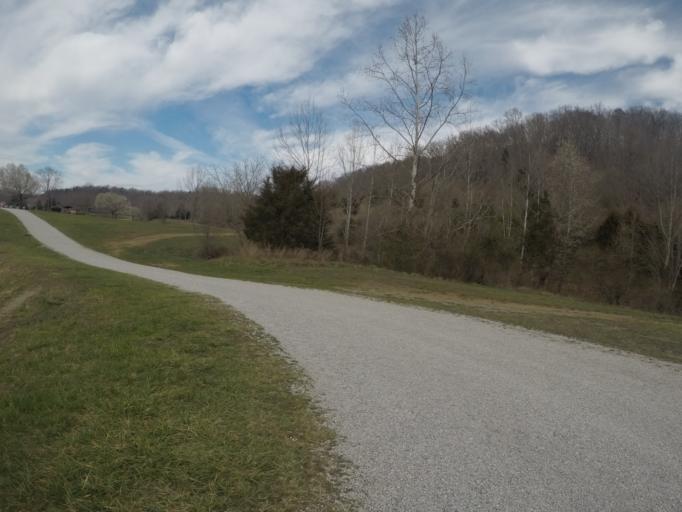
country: US
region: West Virginia
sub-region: Cabell County
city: Barboursville
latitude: 38.3879
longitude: -82.2969
